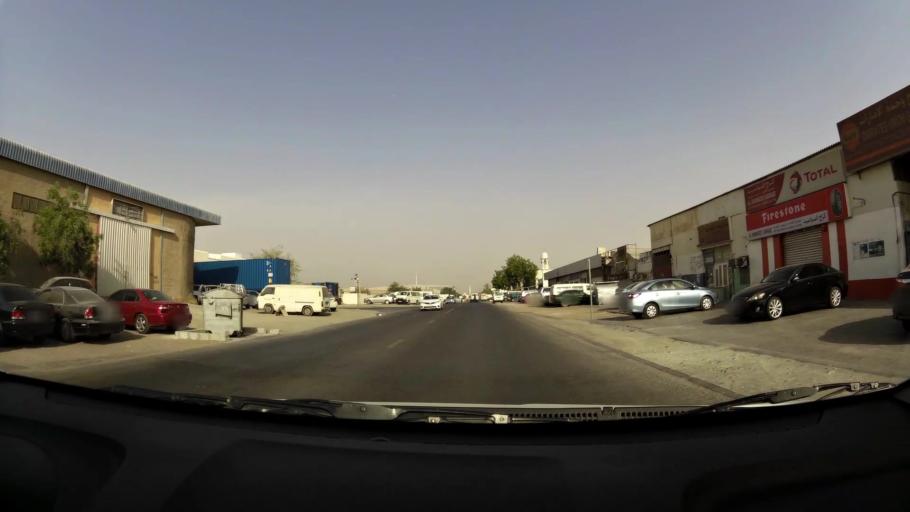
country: AE
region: Ash Shariqah
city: Sharjah
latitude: 25.2274
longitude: 55.3712
